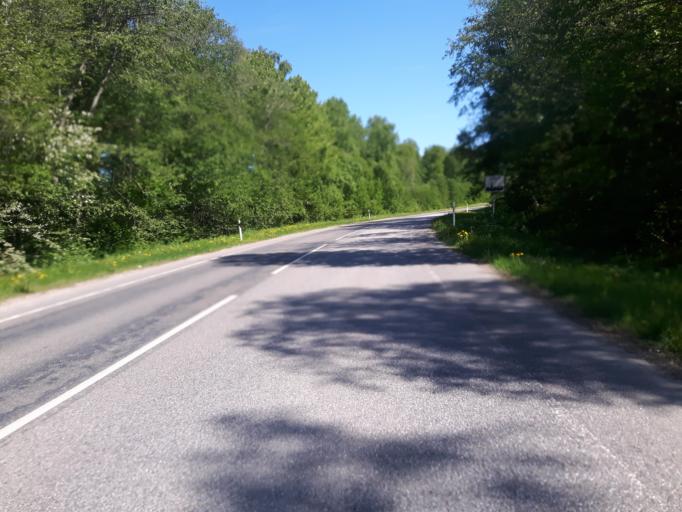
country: EE
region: Ida-Virumaa
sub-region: Aseri vald
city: Aseri
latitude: 59.4485
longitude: 26.8555
